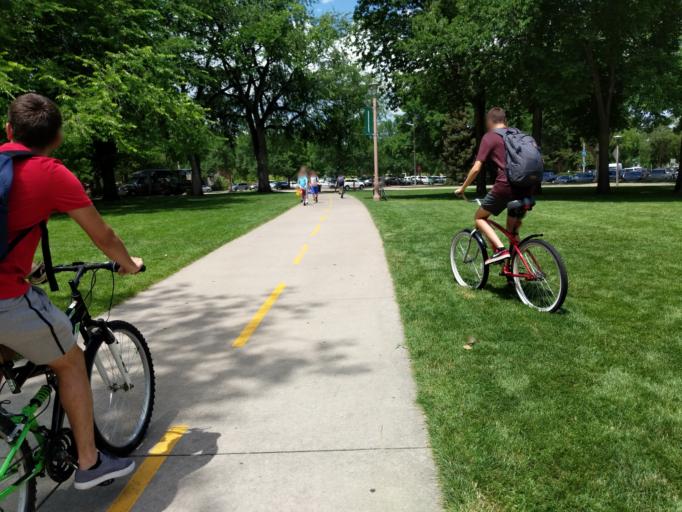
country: US
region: Colorado
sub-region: Larimer County
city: Fort Collins
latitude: 40.5759
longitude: -105.0874
